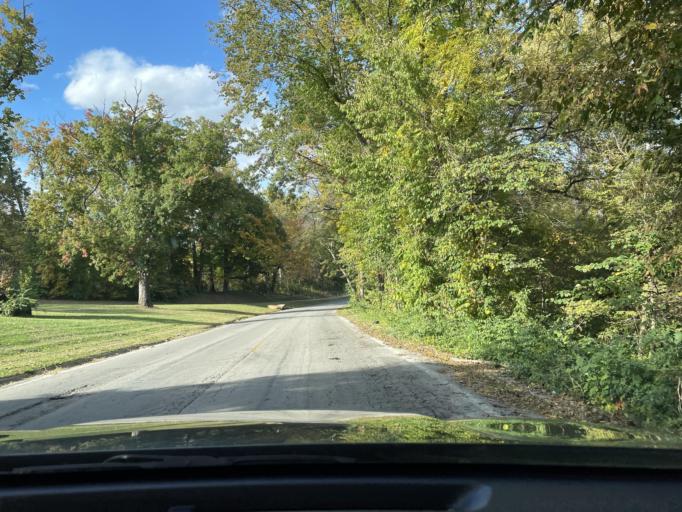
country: US
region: Missouri
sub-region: Buchanan County
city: Saint Joseph
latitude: 39.7328
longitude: -94.8386
